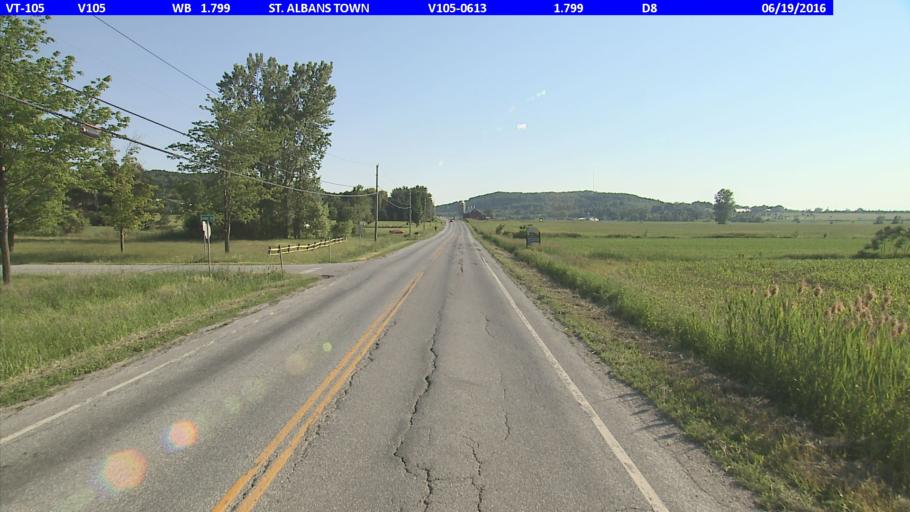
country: US
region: Vermont
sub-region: Franklin County
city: Saint Albans
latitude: 44.8343
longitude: -73.0482
